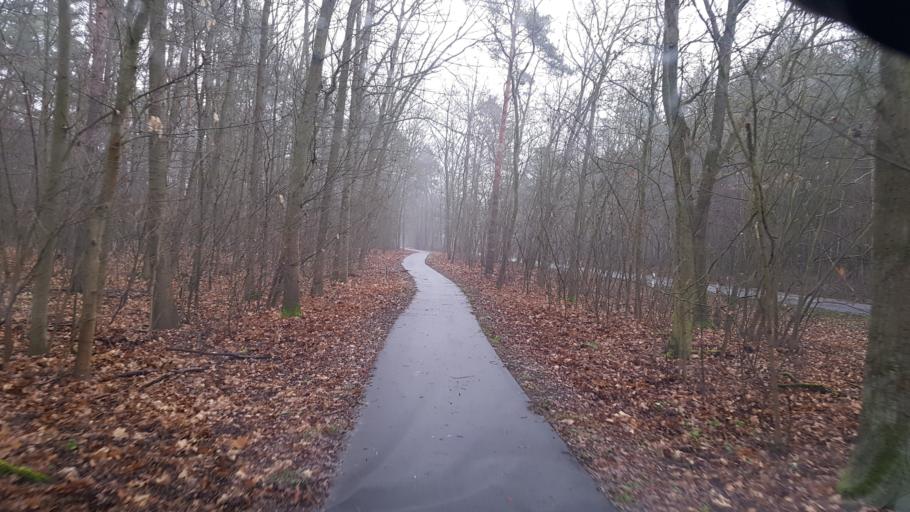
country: DE
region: Brandenburg
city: Stahnsdorf
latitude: 52.3548
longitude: 13.1820
